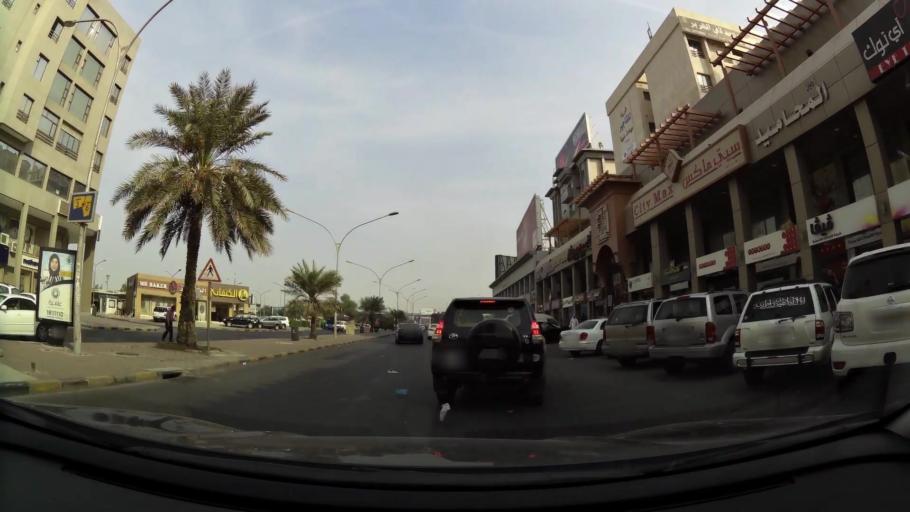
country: KW
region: Al Farwaniyah
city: Al Farwaniyah
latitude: 29.2723
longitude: 47.9666
